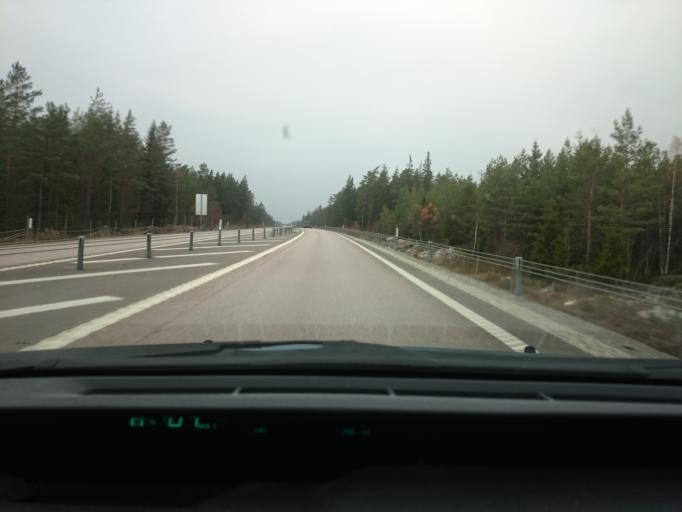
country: SE
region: Vaestmanland
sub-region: Sala Kommun
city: Sala
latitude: 59.9909
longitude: 16.4466
